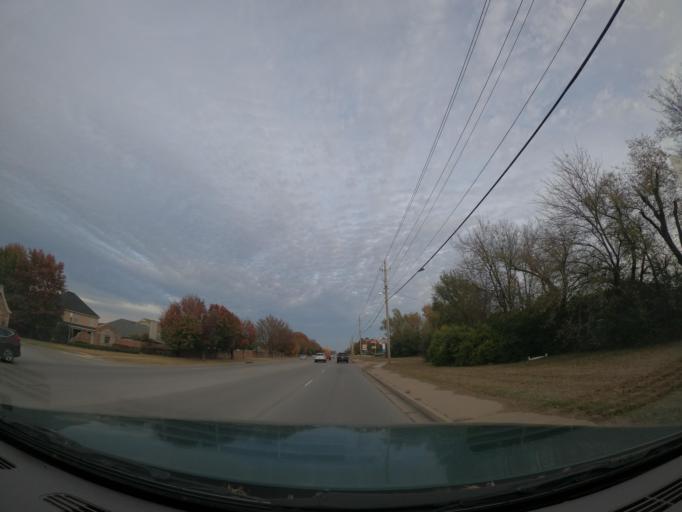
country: US
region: Oklahoma
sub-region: Tulsa County
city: Broken Arrow
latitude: 36.0608
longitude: -95.8279
